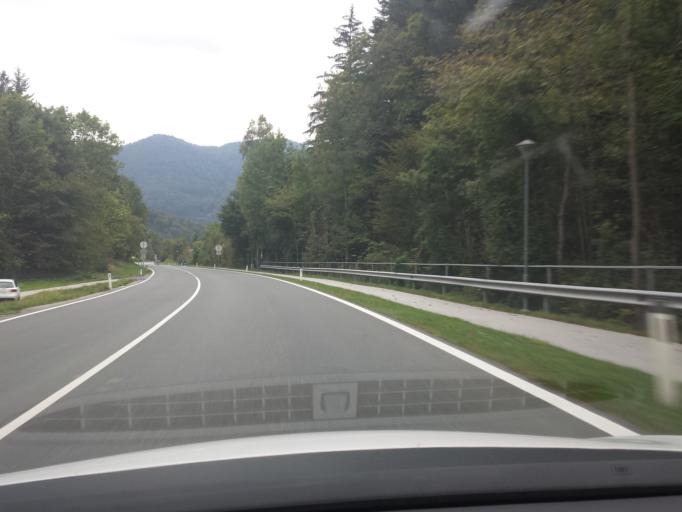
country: AT
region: Salzburg
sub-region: Politischer Bezirk Salzburg-Umgebung
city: Fuschl am See
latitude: 47.7989
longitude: 13.3110
